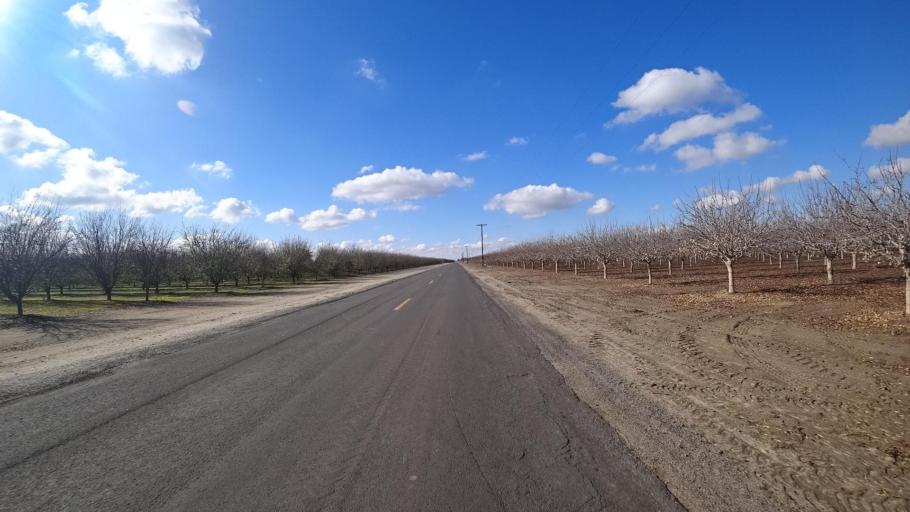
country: US
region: California
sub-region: Kern County
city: Delano
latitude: 35.7323
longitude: -119.3161
